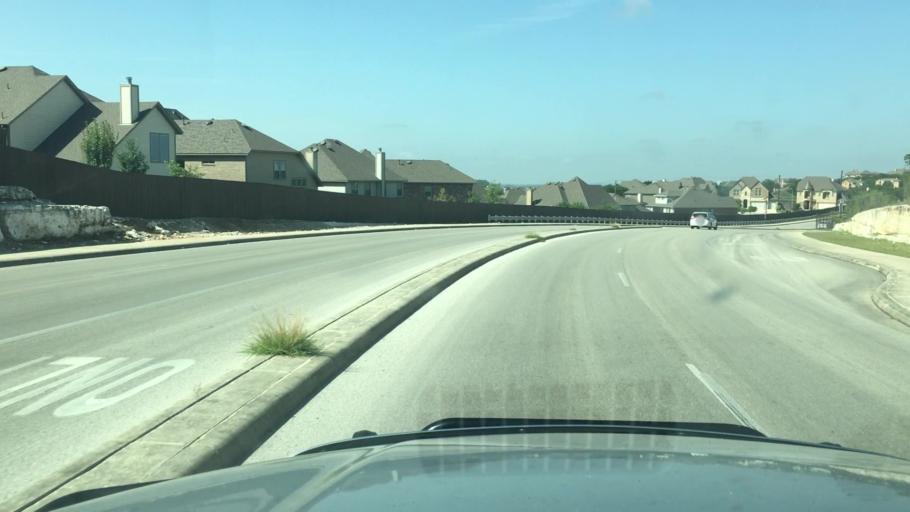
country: US
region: Texas
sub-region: Bexar County
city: Timberwood Park
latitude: 29.6712
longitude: -98.4550
